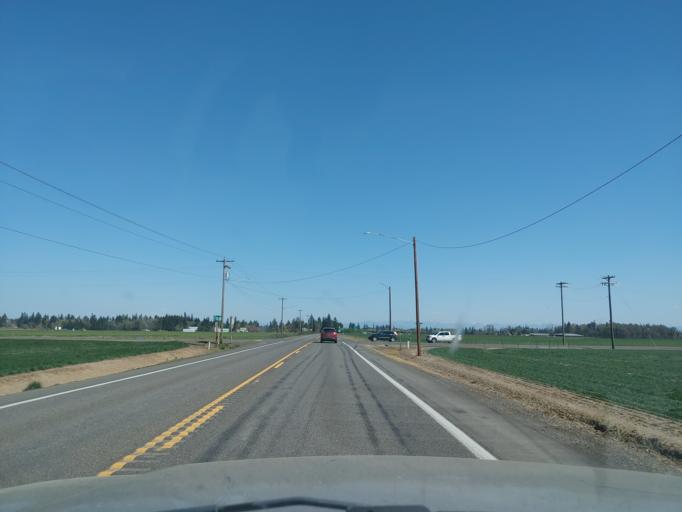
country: US
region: Oregon
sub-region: Marion County
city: Hubbard
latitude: 45.2287
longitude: -122.8795
